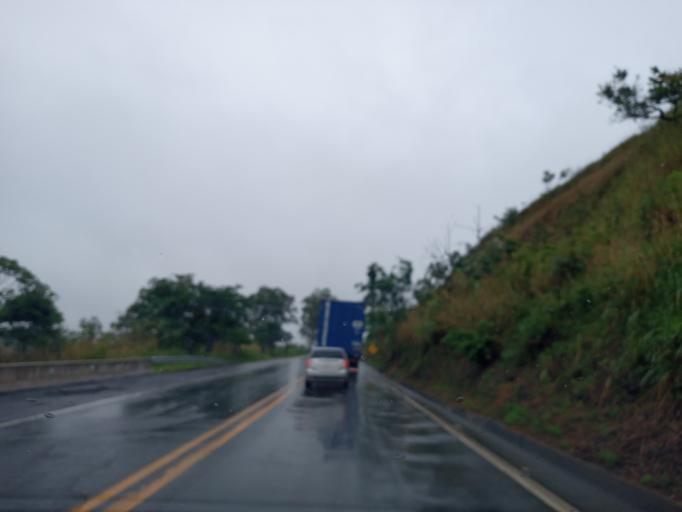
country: BR
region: Minas Gerais
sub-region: Luz
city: Luz
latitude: -19.7191
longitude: -45.8788
